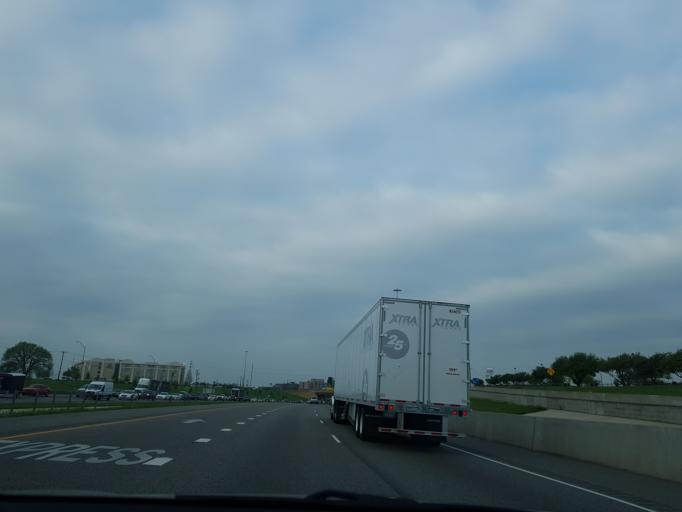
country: US
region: Texas
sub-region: Tarrant County
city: Bedford
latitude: 32.8431
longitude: -97.1172
